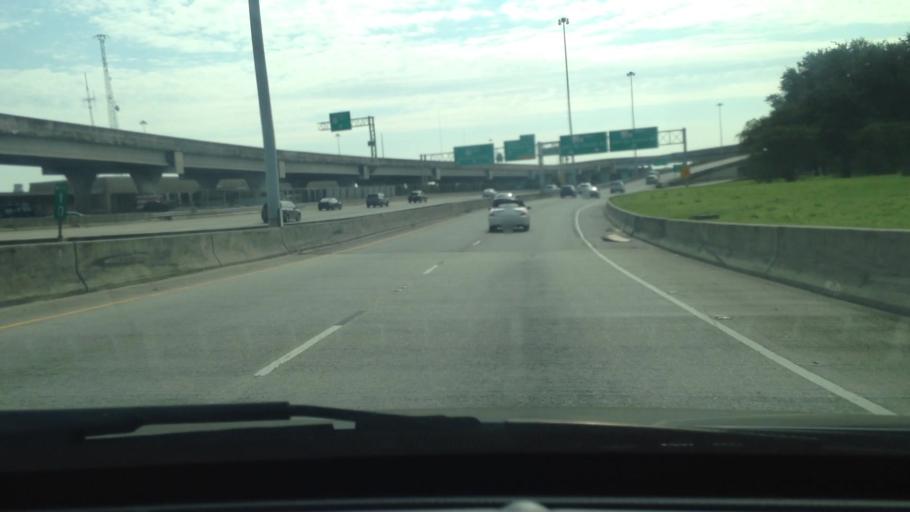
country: US
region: Louisiana
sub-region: Jefferson Parish
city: Gretna
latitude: 29.9354
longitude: -90.0387
